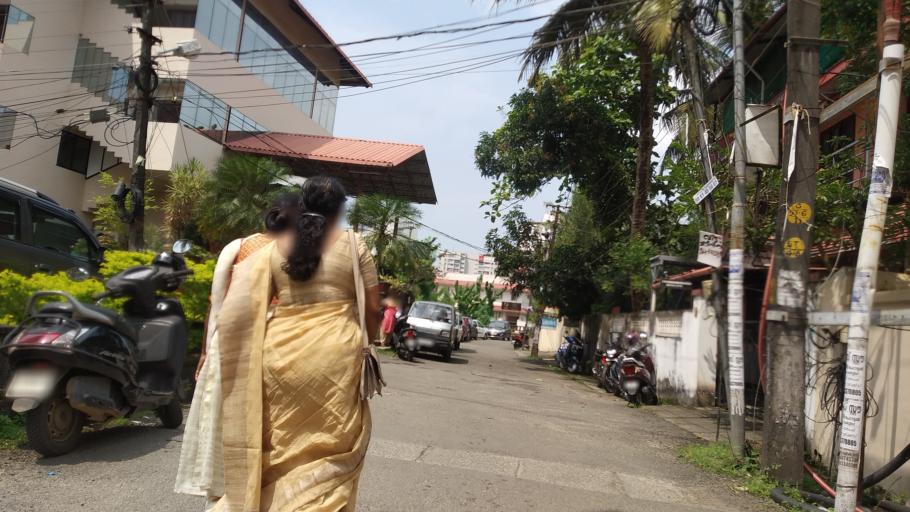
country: IN
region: Kerala
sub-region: Ernakulam
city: Cochin
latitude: 9.9691
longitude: 76.3045
